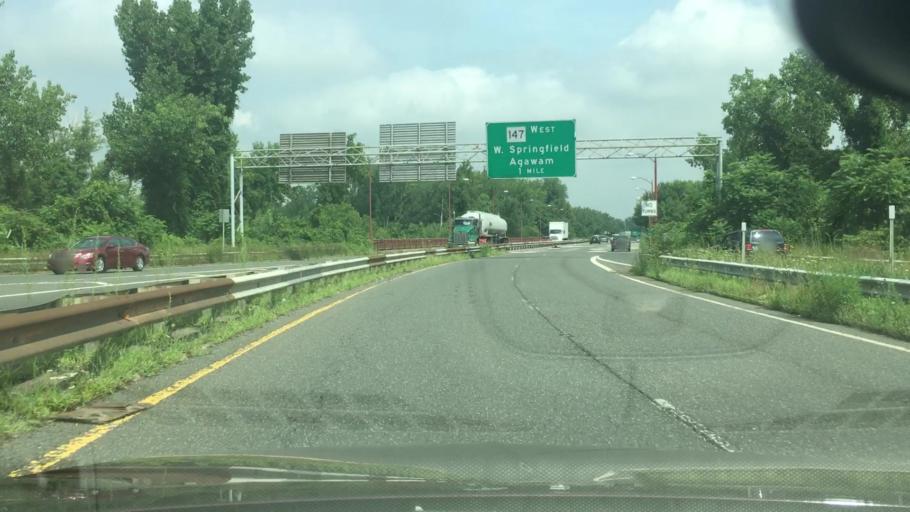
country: US
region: Massachusetts
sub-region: Hampden County
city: Springfield
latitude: 42.0824
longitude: -72.5914
